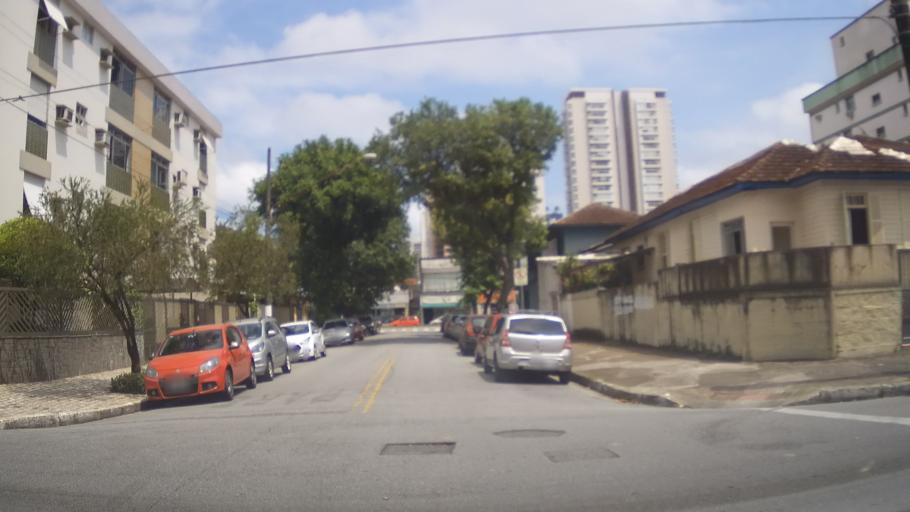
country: BR
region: Sao Paulo
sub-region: Santos
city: Santos
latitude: -23.9678
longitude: -46.3127
